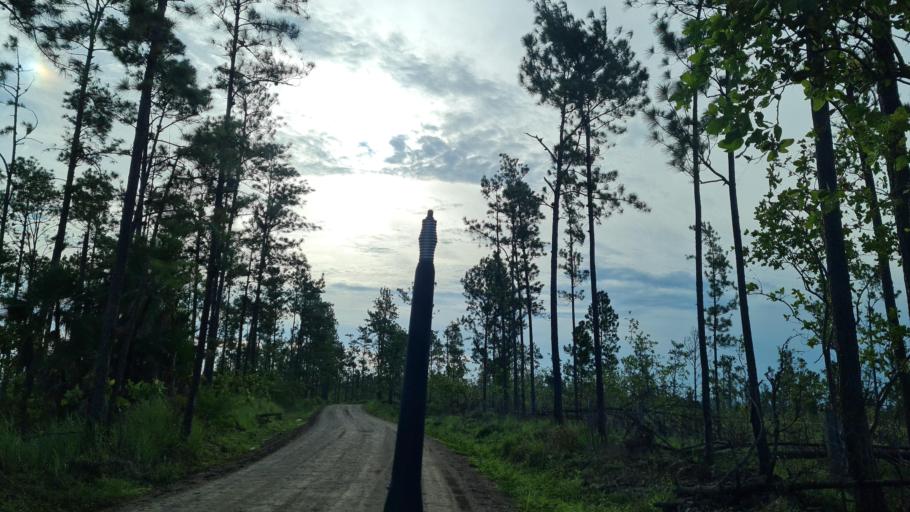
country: NI
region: Atlantico Sur
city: La Cruz de Rio Grande
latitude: 13.5633
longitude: -84.3086
